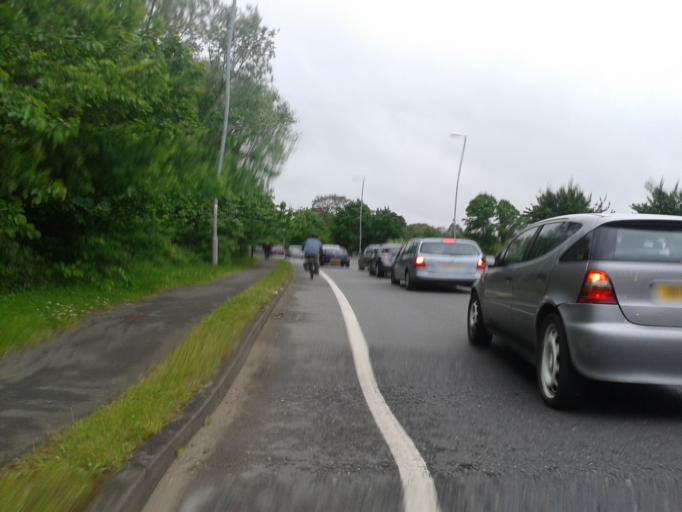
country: GB
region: England
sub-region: Cambridgeshire
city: Histon
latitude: 52.2318
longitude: 0.1117
